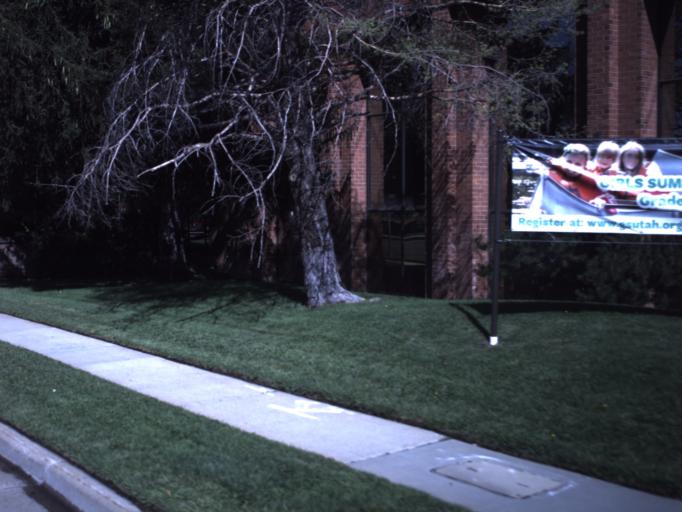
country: US
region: Utah
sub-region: Salt Lake County
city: Murray
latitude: 40.6744
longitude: -111.8780
